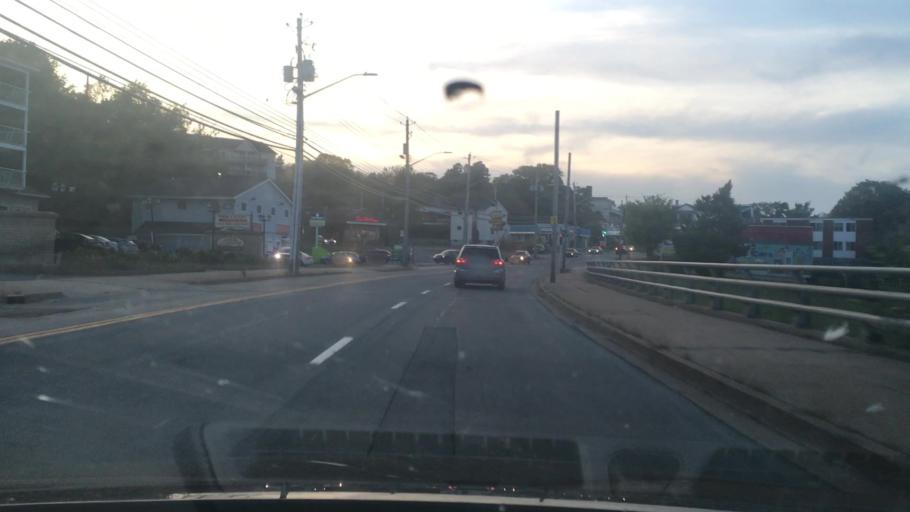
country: CA
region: Nova Scotia
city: Dartmouth
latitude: 44.6742
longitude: -63.6463
